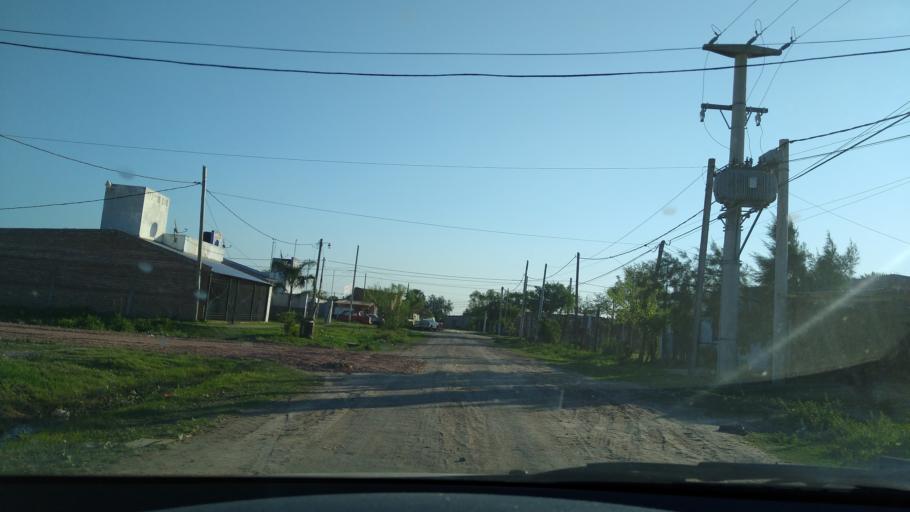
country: AR
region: Chaco
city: Barranqueras
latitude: -27.4927
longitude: -58.9346
